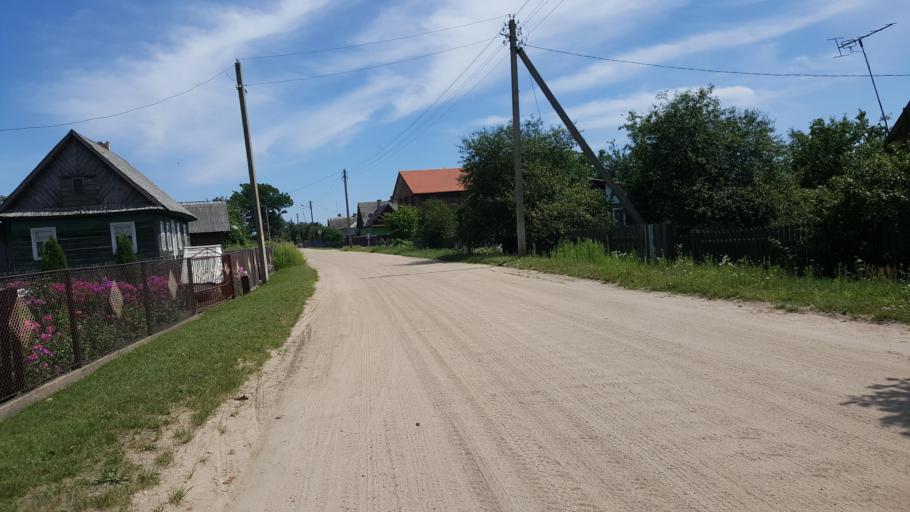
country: BY
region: Brest
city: Pruzhany
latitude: 52.5618
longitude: 24.2088
